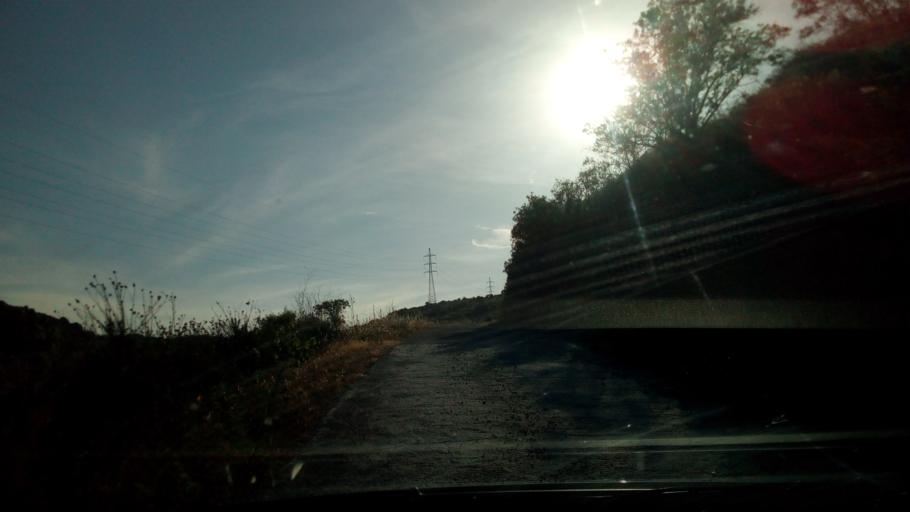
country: CY
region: Pafos
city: Tala
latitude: 34.8721
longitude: 32.4723
